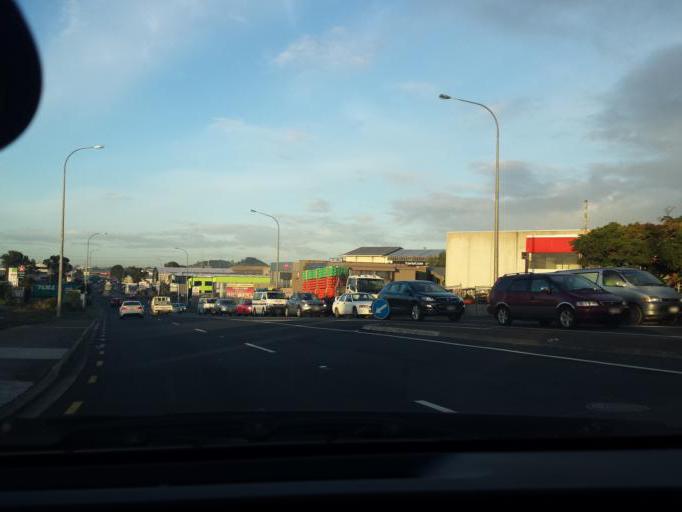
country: NZ
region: Auckland
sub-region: Auckland
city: Mangere
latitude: -36.9205
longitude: 174.8133
